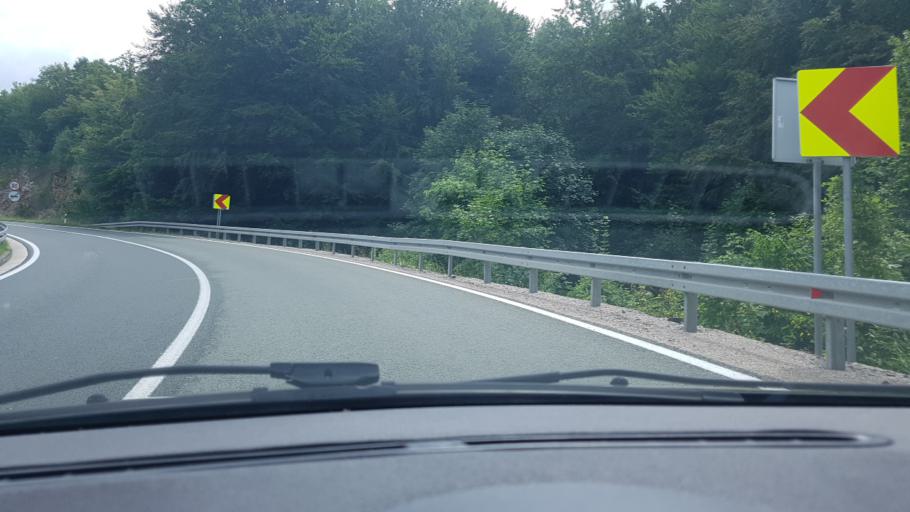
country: HR
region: Licko-Senjska
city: Jezerce
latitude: 44.8844
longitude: 15.6921
